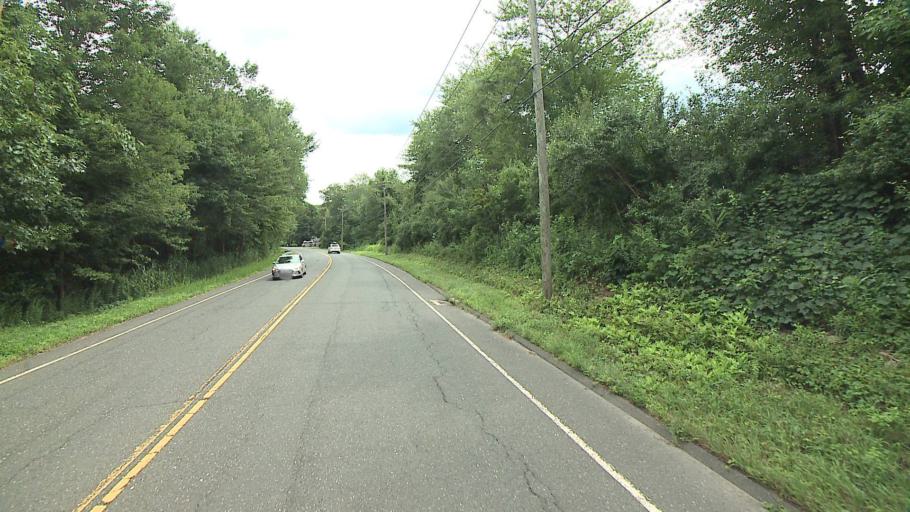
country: US
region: Connecticut
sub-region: Litchfield County
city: Woodbury Center
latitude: 41.5279
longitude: -73.1844
